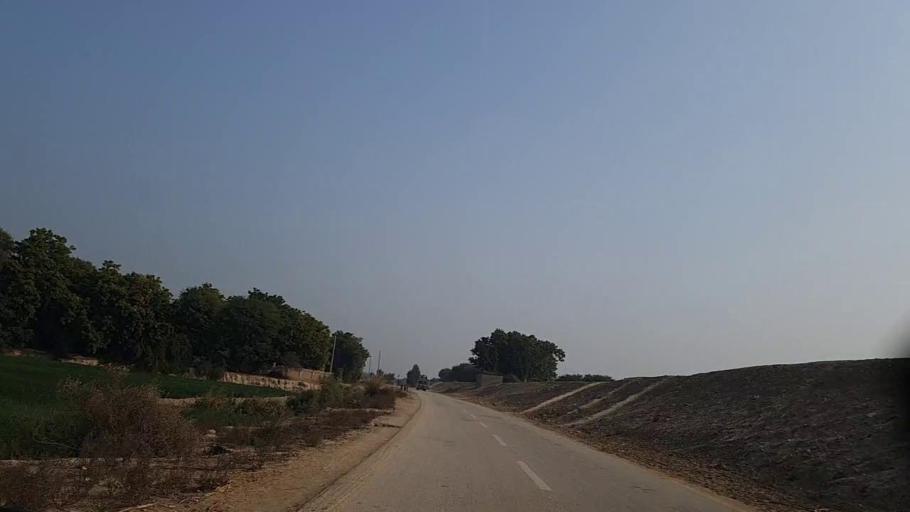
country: PK
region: Sindh
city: Sann
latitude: 26.1539
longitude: 68.1197
